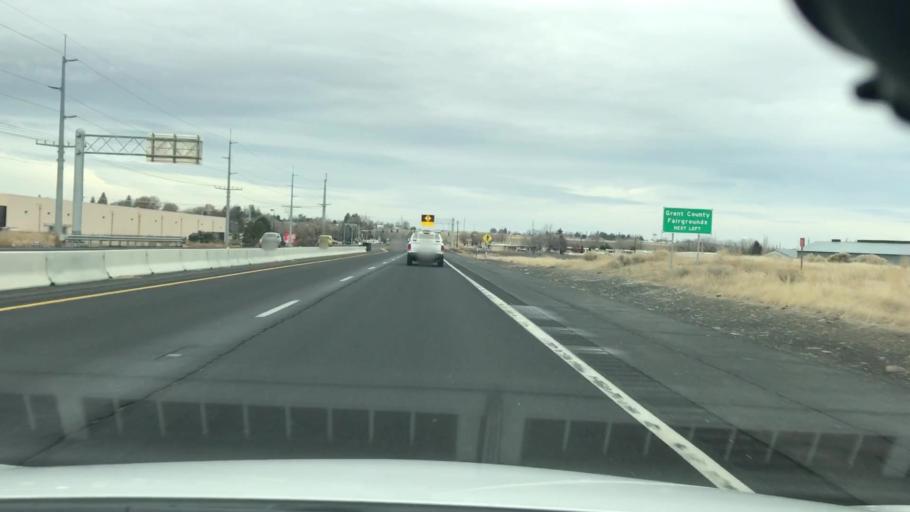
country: US
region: Washington
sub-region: Grant County
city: Moses Lake
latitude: 47.1480
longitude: -119.2895
